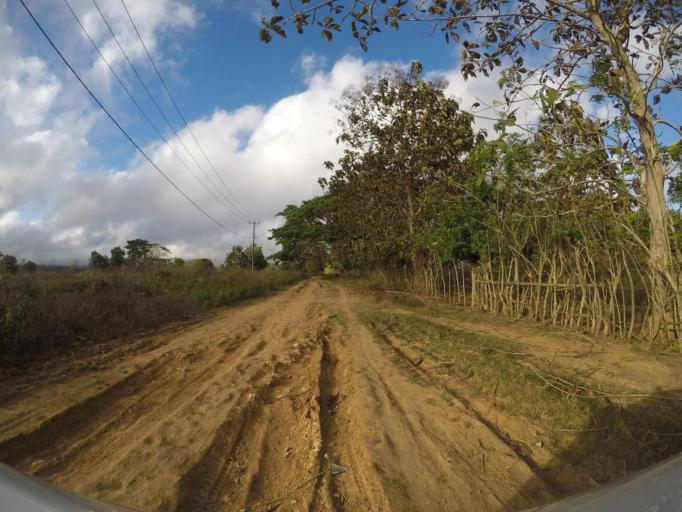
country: TL
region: Lautem
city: Lospalos
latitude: -8.5093
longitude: 126.9935
